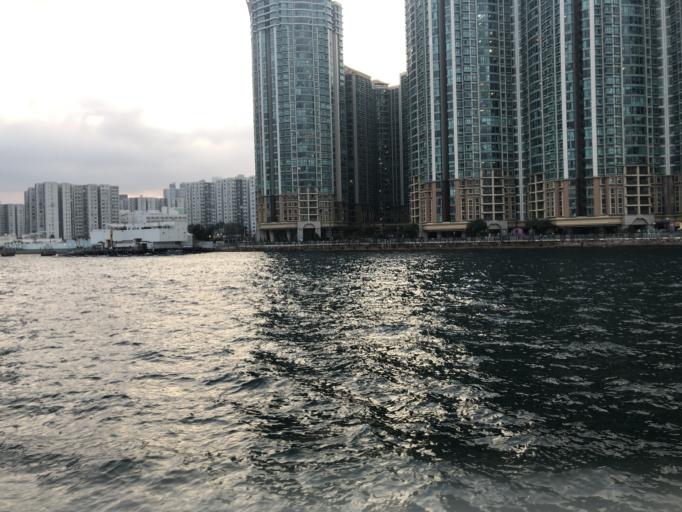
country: HK
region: Kowloon City
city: Kowloon
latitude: 22.3076
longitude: 114.1953
